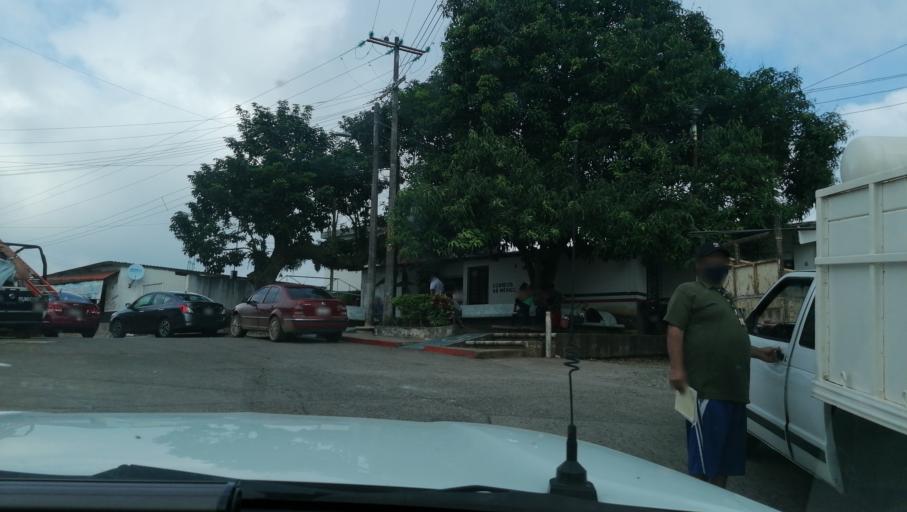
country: MX
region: Chiapas
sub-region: Juarez
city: El Triunfo 1ra. Seccion (Cardona)
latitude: 17.6084
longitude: -93.1932
